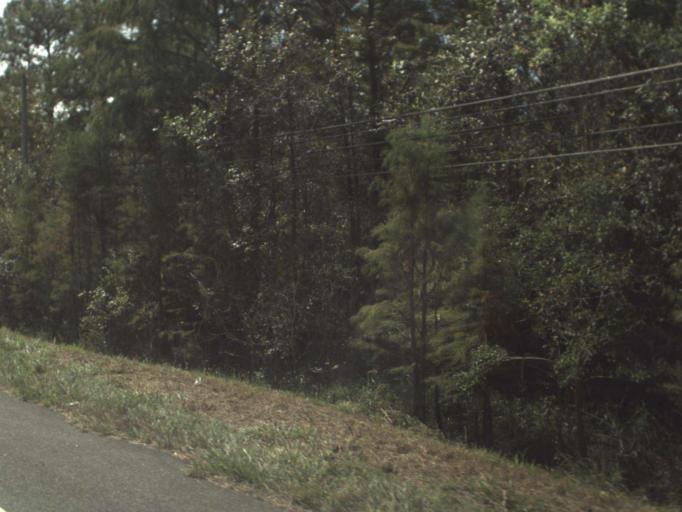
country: US
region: Florida
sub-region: Washington County
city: Chipley
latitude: 30.8240
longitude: -85.5331
